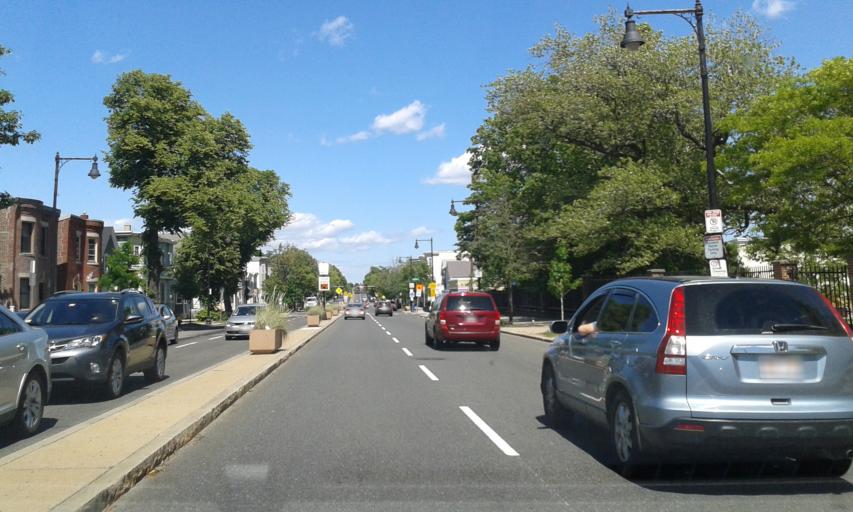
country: US
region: Massachusetts
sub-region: Suffolk County
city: Chelsea
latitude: 42.3813
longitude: -71.0218
